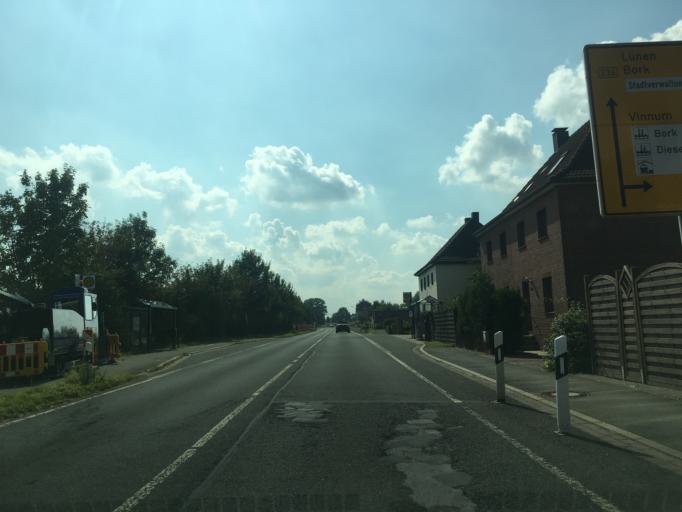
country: DE
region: North Rhine-Westphalia
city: Selm
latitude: 51.6739
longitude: 7.4708
